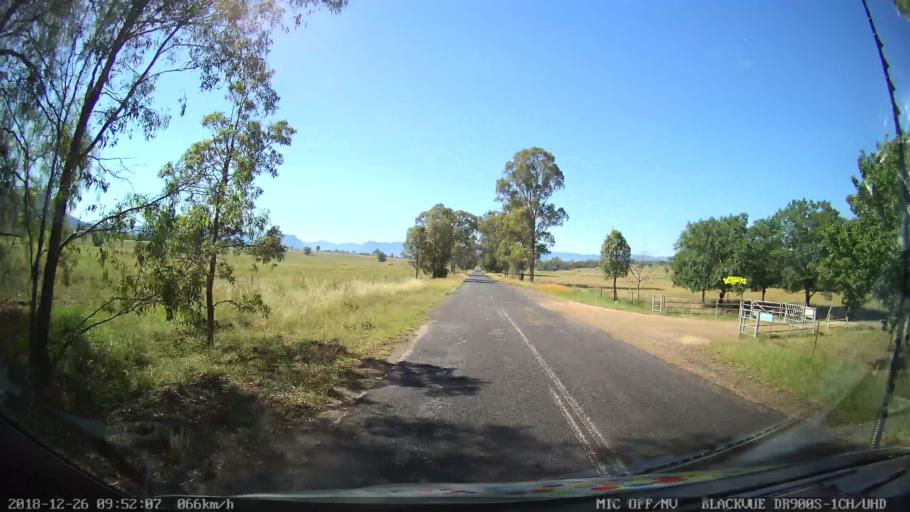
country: AU
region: New South Wales
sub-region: Mid-Western Regional
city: Kandos
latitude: -33.0075
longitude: 150.1476
